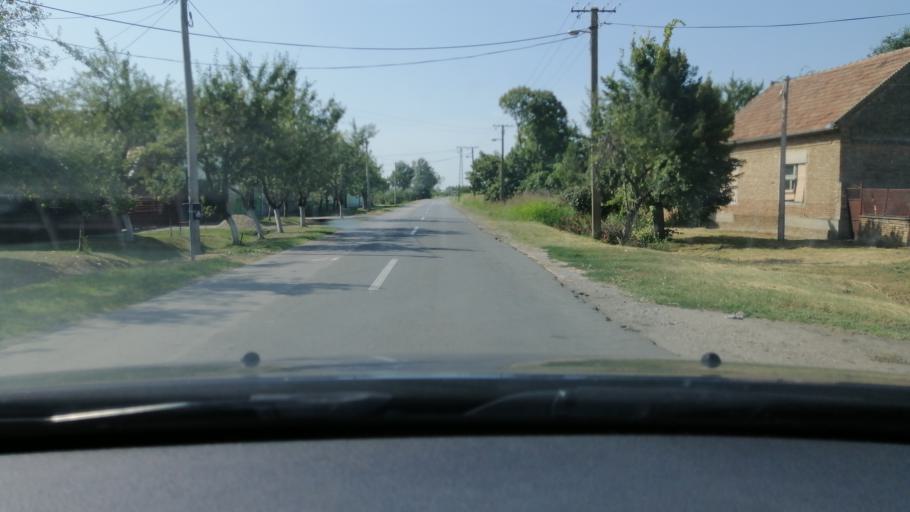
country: RS
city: Tomasevac
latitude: 45.2609
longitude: 20.6174
